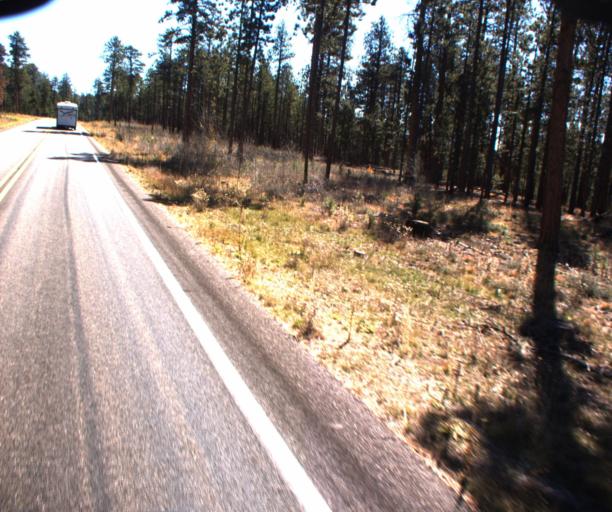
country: US
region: Arizona
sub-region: Coconino County
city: Fredonia
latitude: 36.6461
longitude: -112.1808
